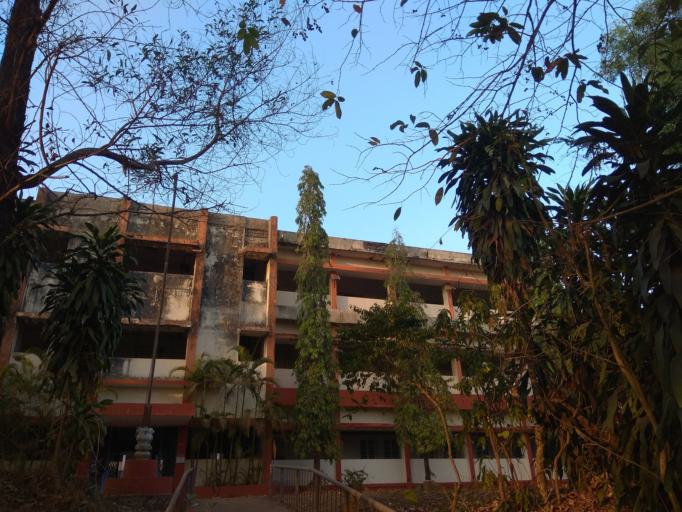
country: IN
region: Karnataka
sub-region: Dakshina Kannada
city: Mangalore
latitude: 12.9239
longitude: 74.8676
